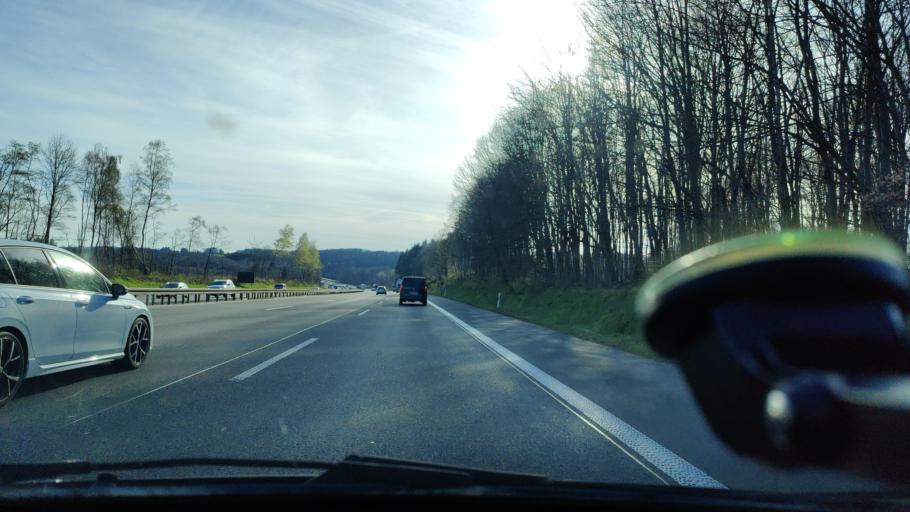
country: DE
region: North Rhine-Westphalia
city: Burscheid
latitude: 51.1228
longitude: 7.1643
